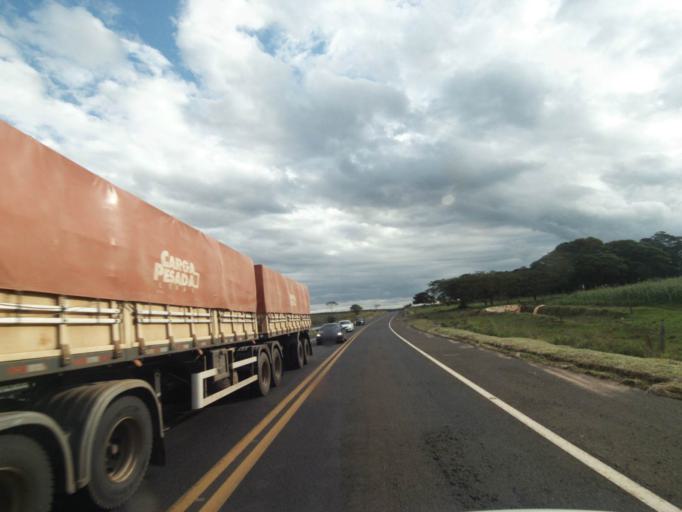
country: PY
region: Canindeyu
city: Salto del Guaira
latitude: -24.0831
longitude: -54.0695
